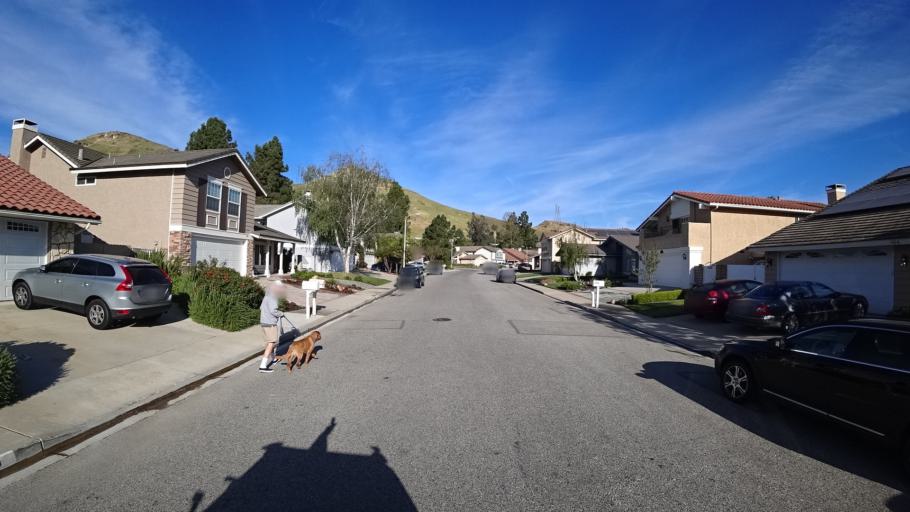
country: US
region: California
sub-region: Ventura County
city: Casa Conejo
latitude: 34.1910
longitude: -118.9581
